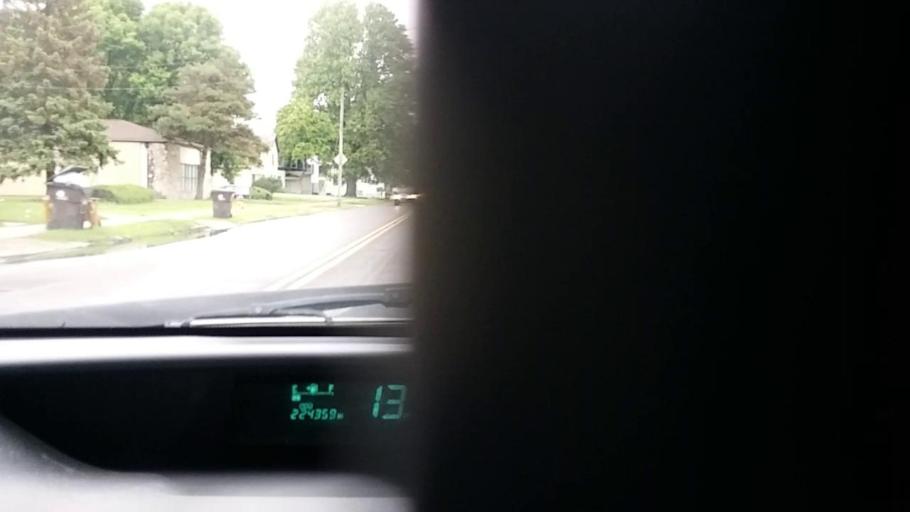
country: US
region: Illinois
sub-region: Peoria County
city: Peoria
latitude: 40.7015
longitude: -89.6036
